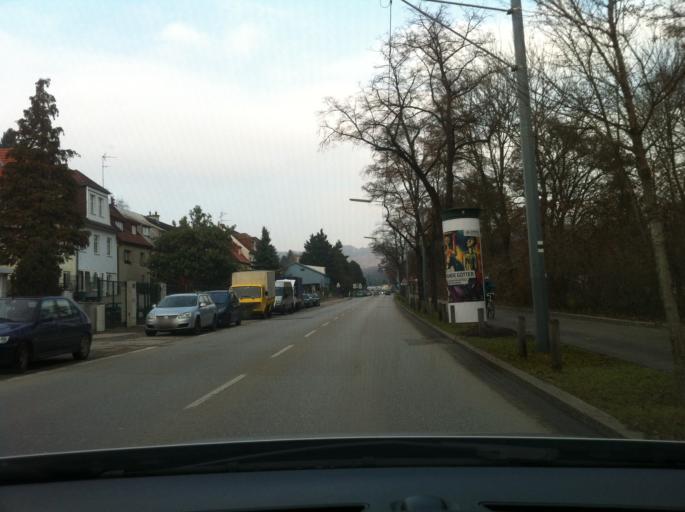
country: AT
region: Lower Austria
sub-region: Politischer Bezirk Wien-Umgebung
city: Purkersdorf
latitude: 48.2153
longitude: 16.2492
